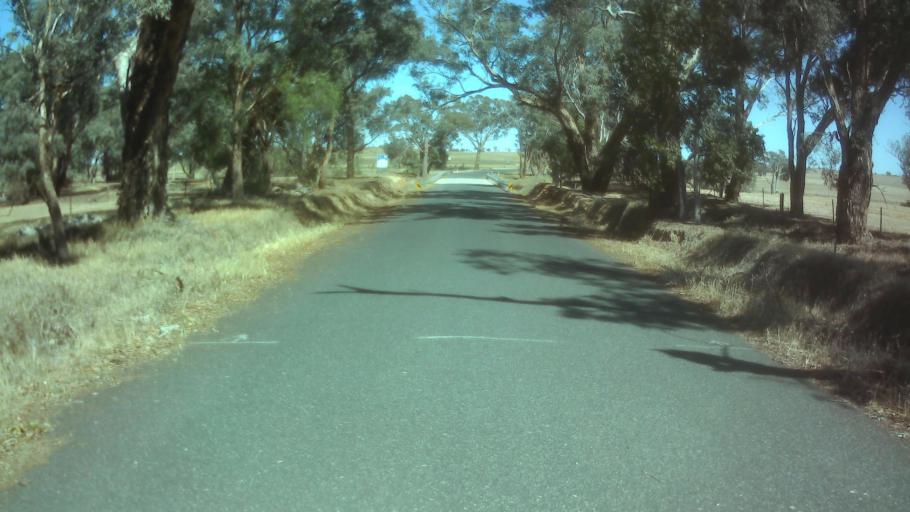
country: AU
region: New South Wales
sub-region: Weddin
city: Grenfell
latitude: -33.9853
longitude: 148.4082
